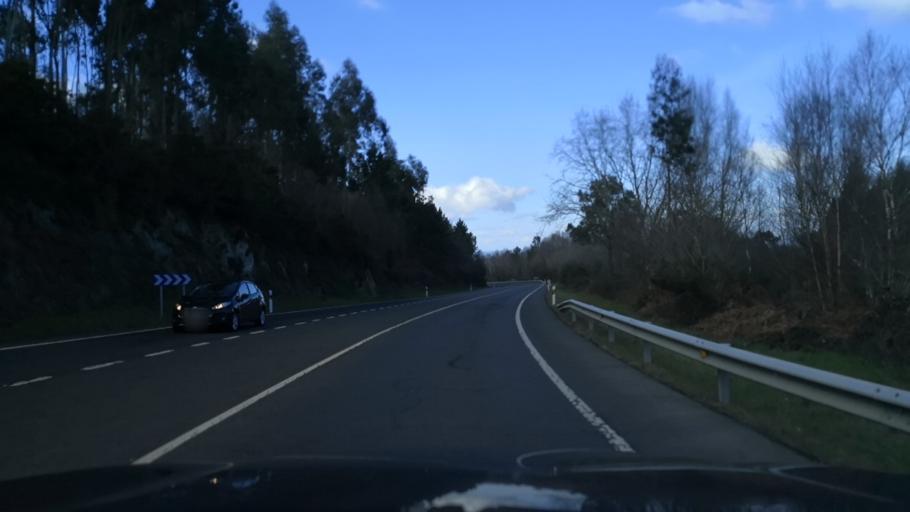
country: ES
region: Galicia
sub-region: Provincia da Coruna
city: Ribeira
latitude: 42.7119
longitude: -8.3585
